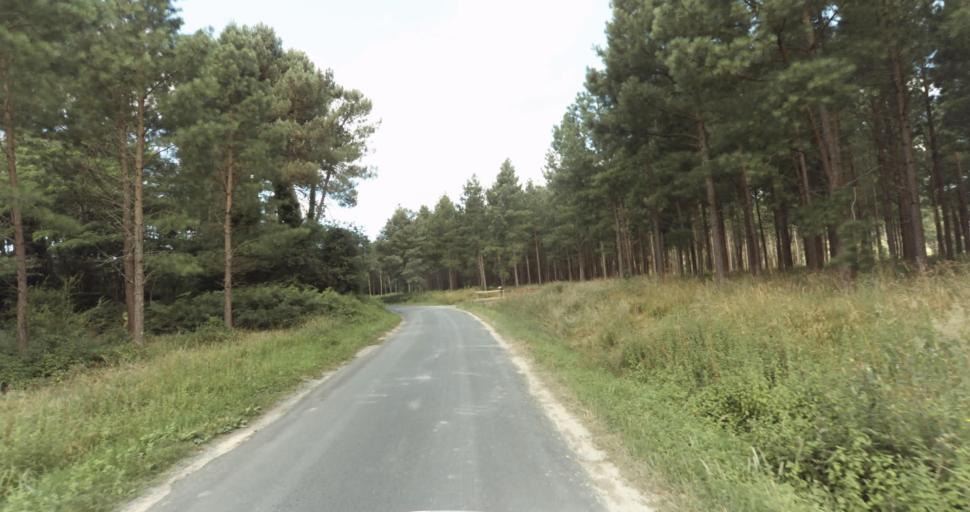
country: FR
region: Aquitaine
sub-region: Departement de la Gironde
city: Bazas
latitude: 44.4505
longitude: -0.2214
